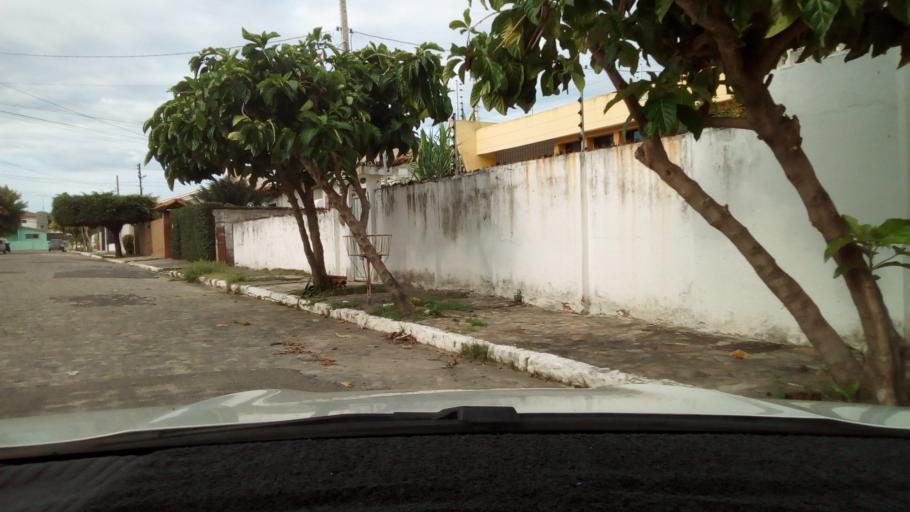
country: BR
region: Paraiba
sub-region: Joao Pessoa
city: Joao Pessoa
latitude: -7.1139
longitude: -34.8388
